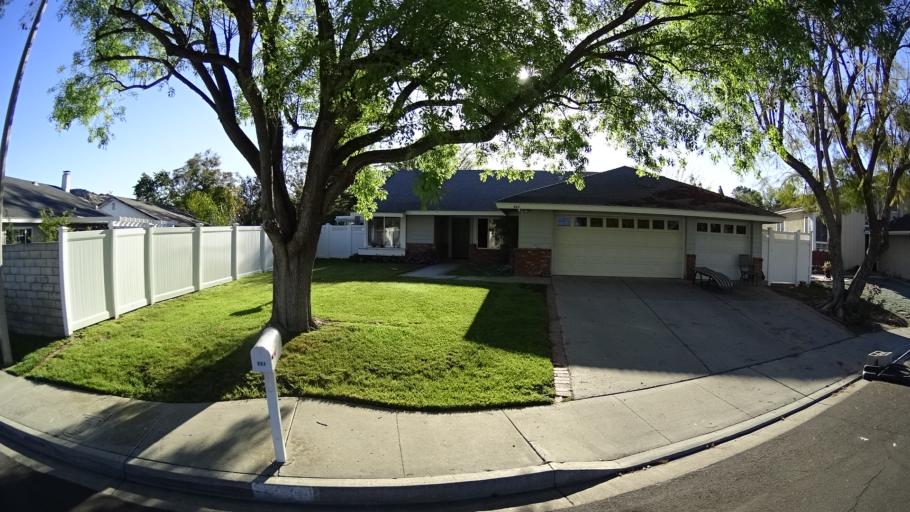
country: US
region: California
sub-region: Ventura County
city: Casa Conejo
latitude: 34.2188
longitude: -118.8940
